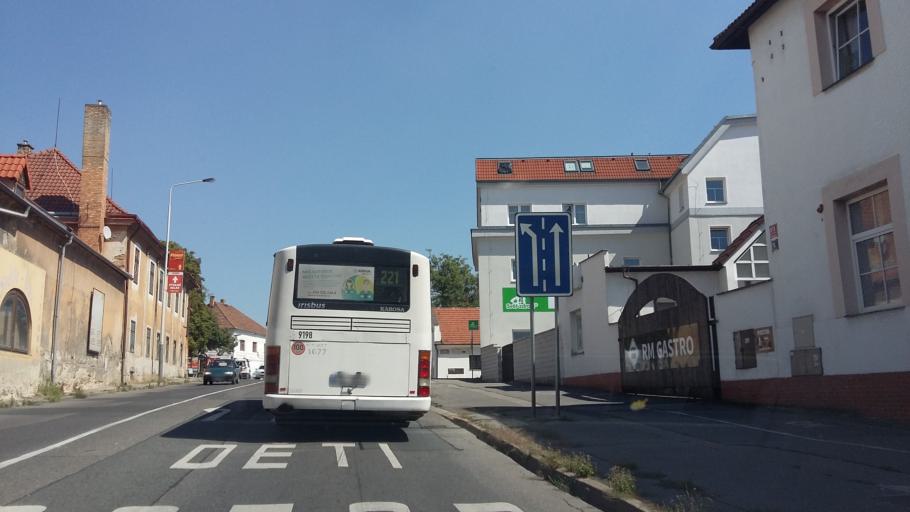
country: CZ
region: Praha
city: Cerny Most
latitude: 50.1120
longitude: 14.5934
